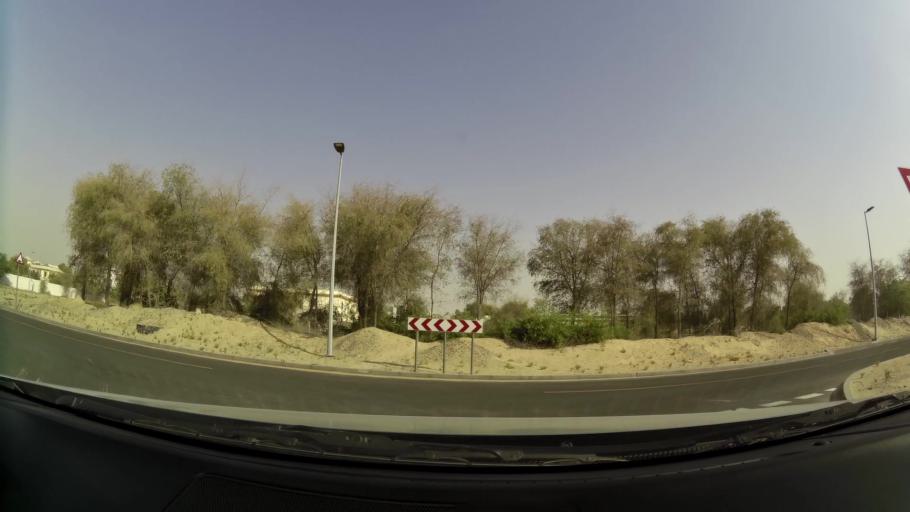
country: AE
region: Dubai
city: Dubai
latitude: 25.1488
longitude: 55.3179
